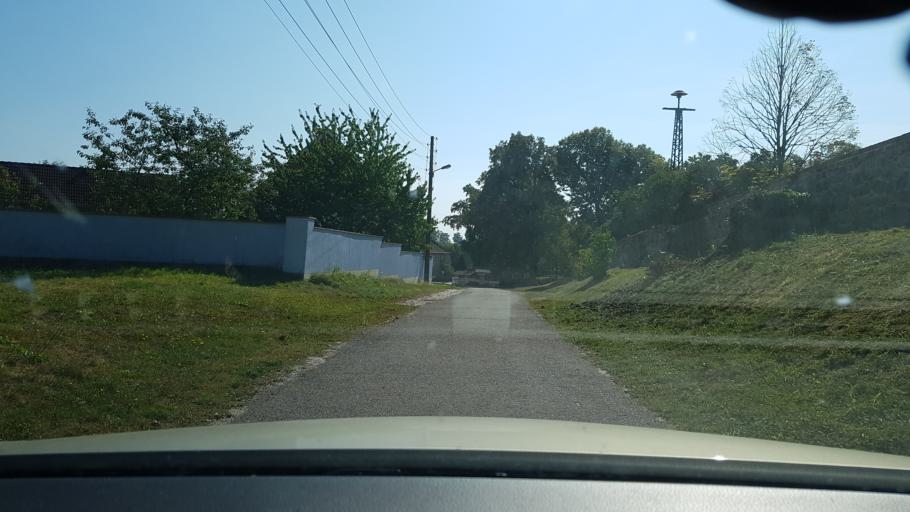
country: DE
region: Brandenburg
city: Lawitz
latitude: 52.1032
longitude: 14.5912
